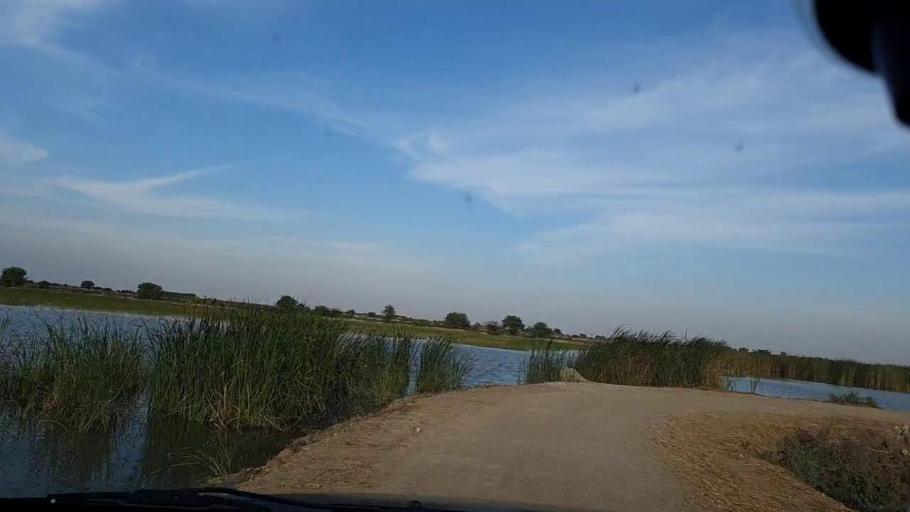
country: PK
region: Sindh
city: Mirpur Batoro
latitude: 24.6586
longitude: 68.2974
